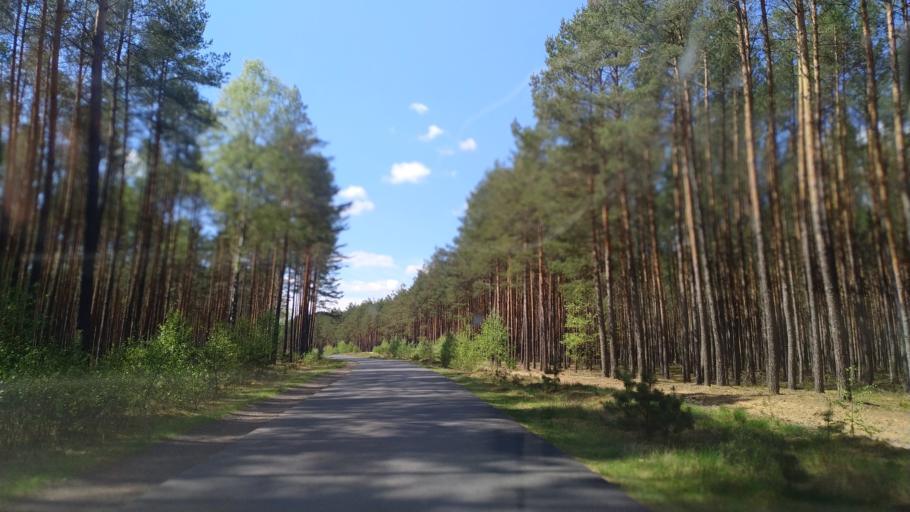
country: PL
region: Greater Poland Voivodeship
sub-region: Powiat zlotowski
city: Tarnowka
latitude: 53.2716
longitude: 16.8615
